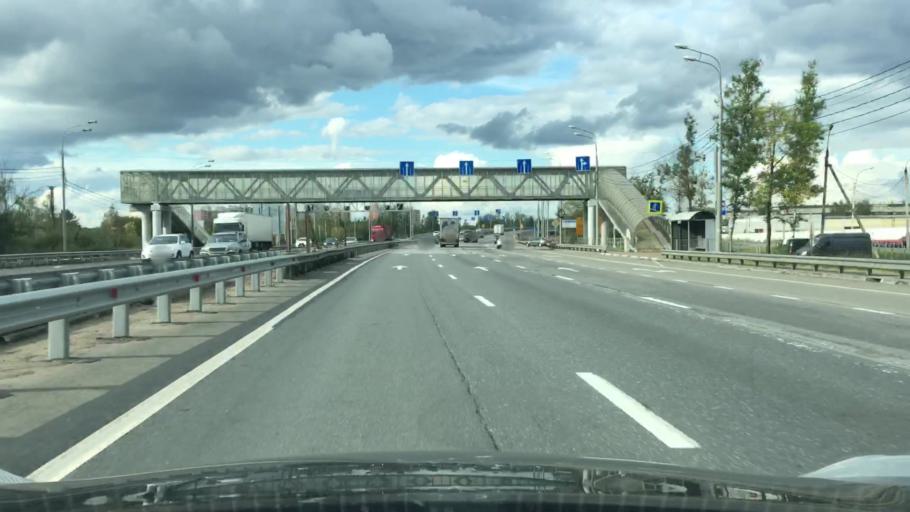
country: RU
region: Tverskaya
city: Tver
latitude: 56.8373
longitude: 35.7956
